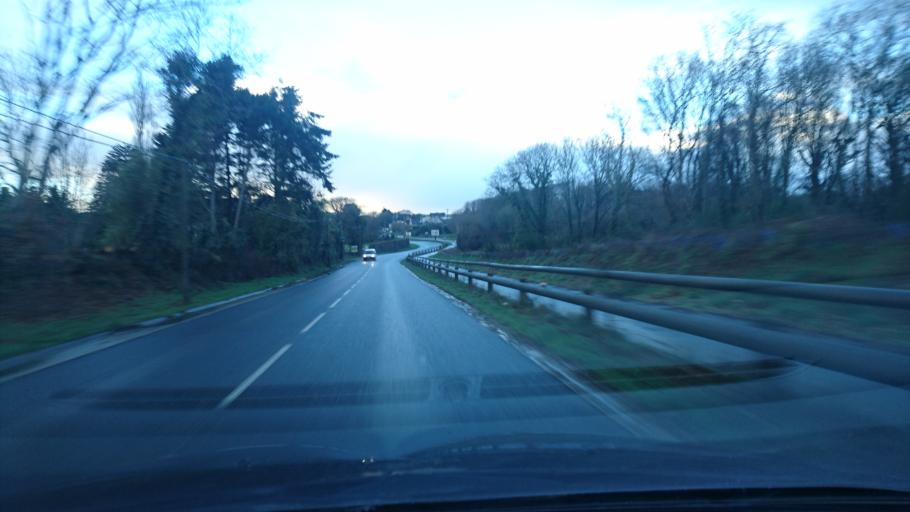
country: FR
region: Brittany
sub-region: Departement du Finistere
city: Guilers
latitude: 48.4150
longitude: -4.5598
